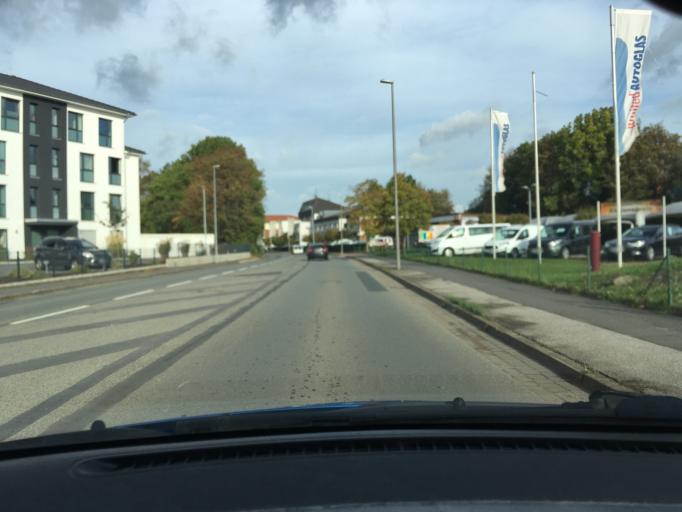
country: DE
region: Lower Saxony
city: Barsinghausen
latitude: 52.3024
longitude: 9.4693
